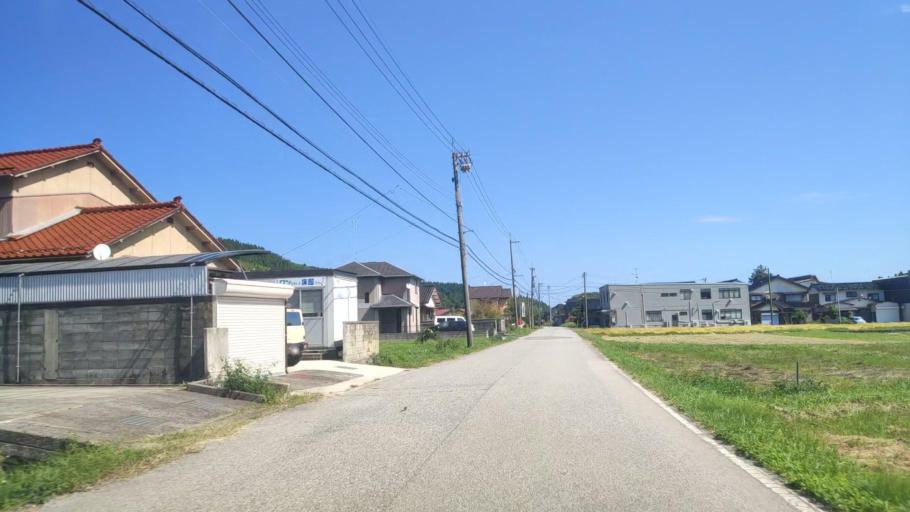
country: JP
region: Ishikawa
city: Nanao
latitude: 37.3762
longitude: 136.8770
